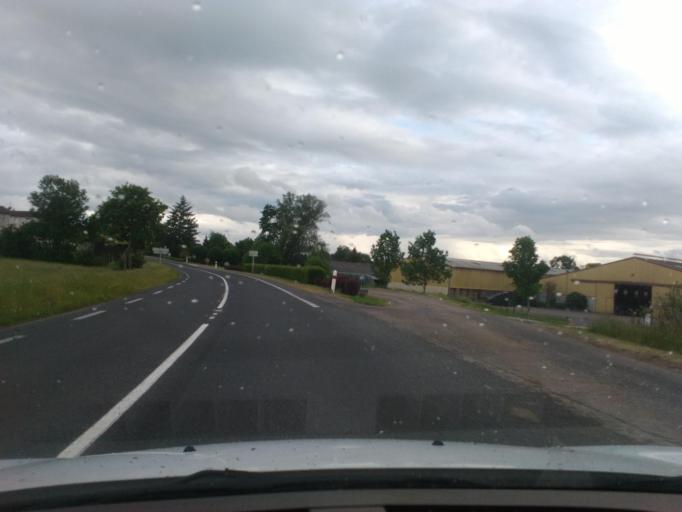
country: FR
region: Lorraine
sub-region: Departement de Meurthe-et-Moselle
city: Gerbeviller
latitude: 48.4520
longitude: 6.5623
